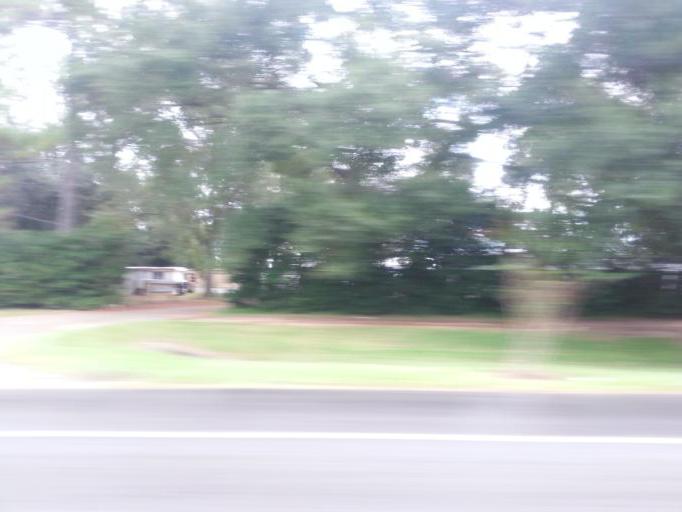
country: US
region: Alabama
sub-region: Baldwin County
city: Fairhope
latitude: 30.5396
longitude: -87.8870
